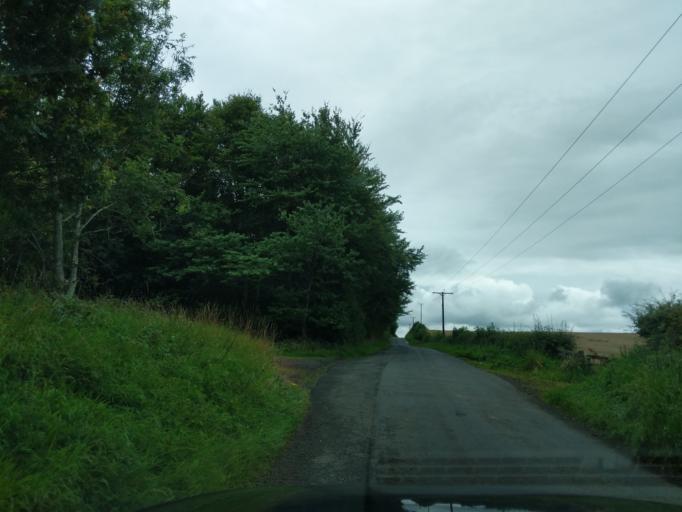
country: GB
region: Scotland
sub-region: Fife
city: Limekilns
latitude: 55.9851
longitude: -3.4893
